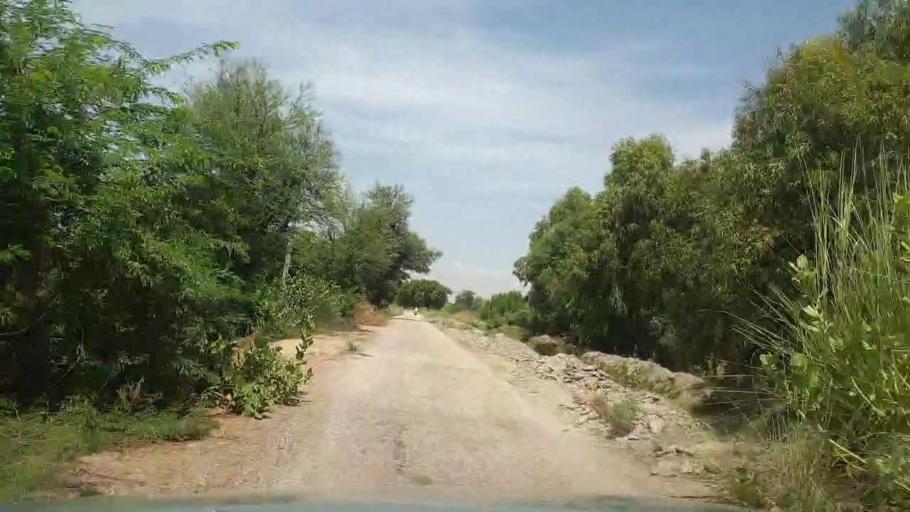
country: PK
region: Sindh
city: Bozdar
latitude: 27.0888
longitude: 69.0082
